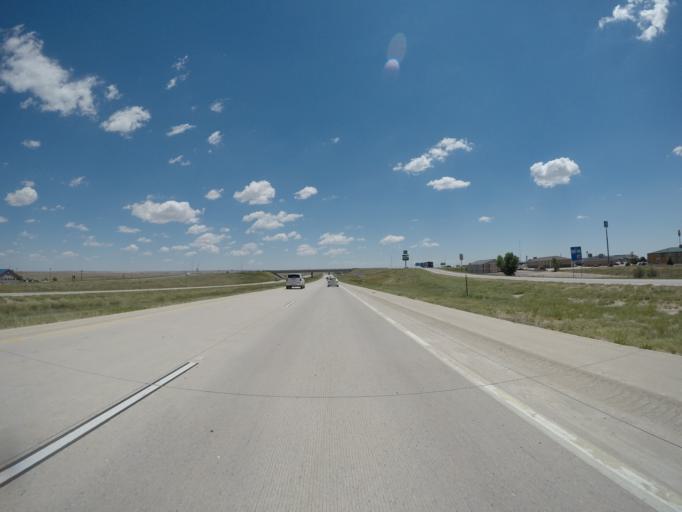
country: US
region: Colorado
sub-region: Lincoln County
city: Limon
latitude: 39.2732
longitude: -103.7103
